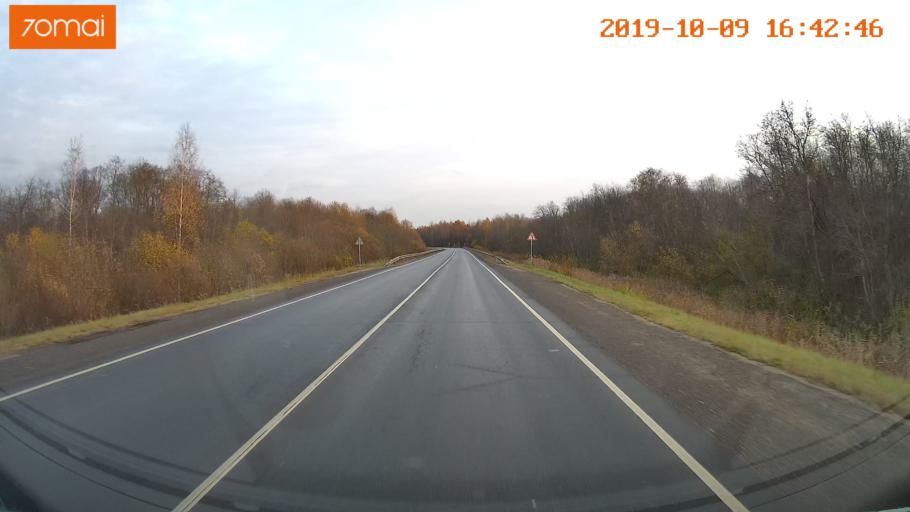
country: RU
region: Kostroma
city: Volgorechensk
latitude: 57.4586
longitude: 41.1073
